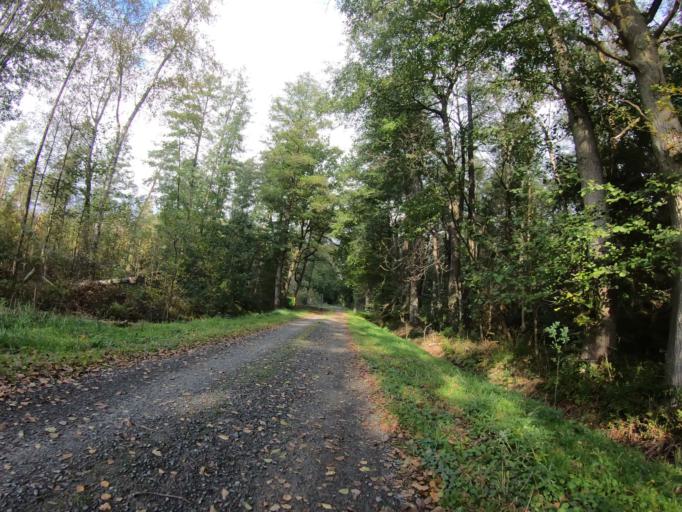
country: DE
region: Lower Saxony
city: Wahrenholz
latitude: 52.5906
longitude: 10.6298
